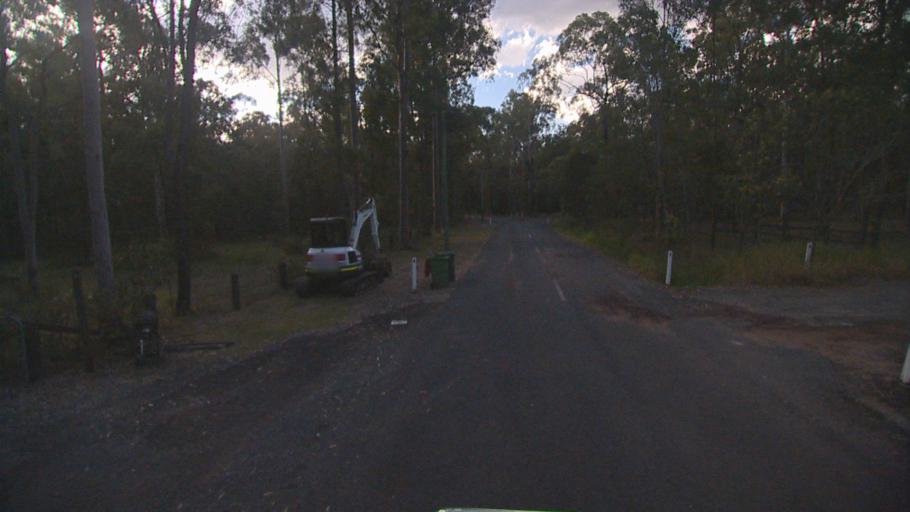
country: AU
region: Queensland
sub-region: Ipswich
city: Springfield Lakes
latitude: -27.6920
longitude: 152.9544
